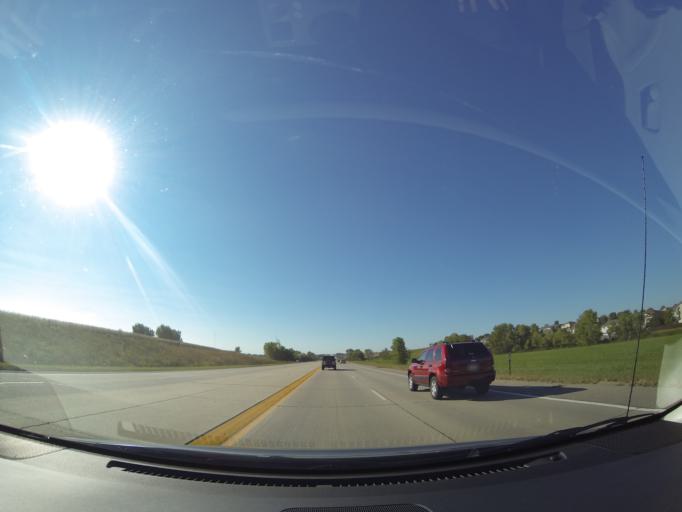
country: US
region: Nebraska
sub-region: Sarpy County
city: Gretna
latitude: 41.1235
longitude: -96.2533
